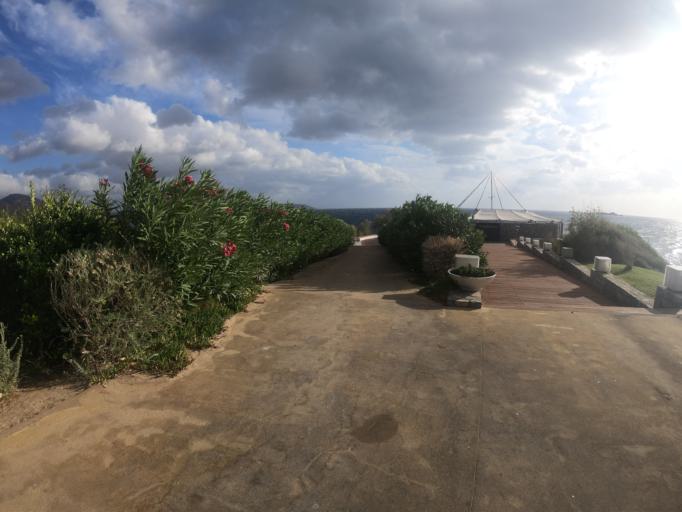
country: GR
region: Attica
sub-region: Nomarchia Anatolikis Attikis
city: Saronida
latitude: 37.7740
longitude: 23.8863
